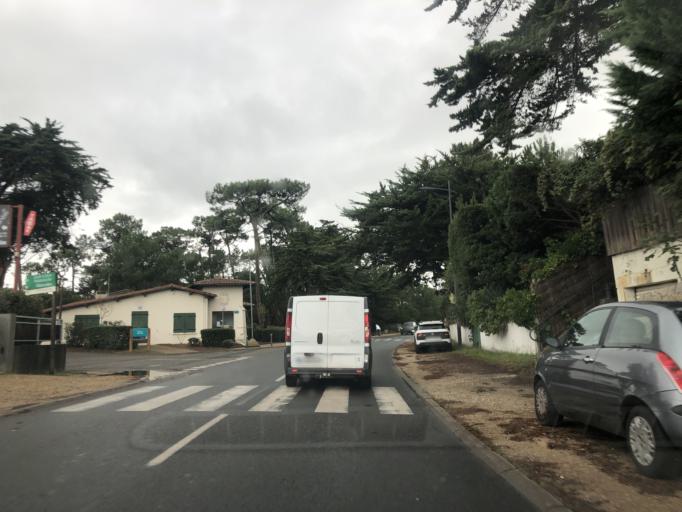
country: FR
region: Aquitaine
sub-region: Departement de la Gironde
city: Arcachon
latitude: 44.6986
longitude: -1.2299
